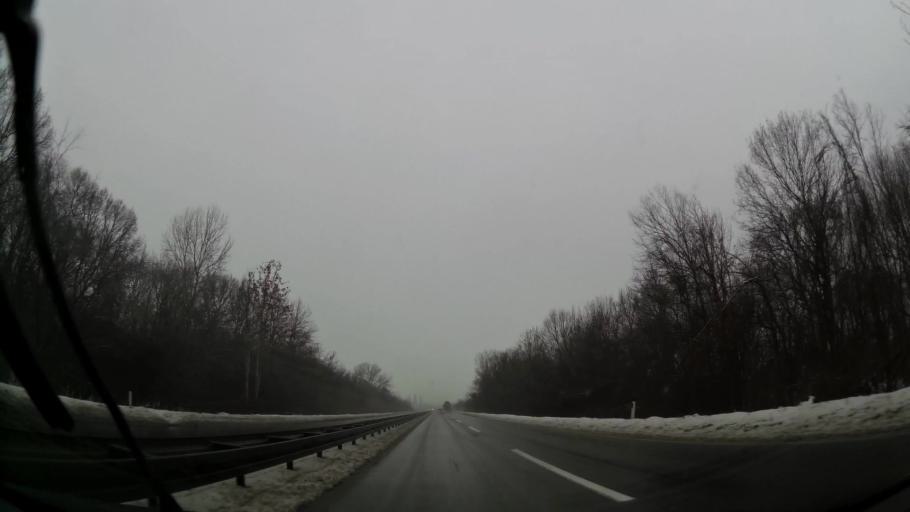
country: RS
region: Central Serbia
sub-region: Belgrade
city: Cukarica
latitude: 44.7666
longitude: 20.3920
